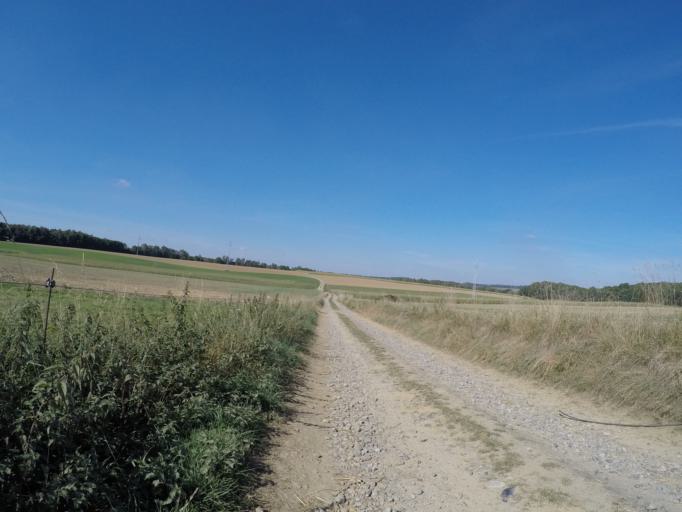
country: BE
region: Wallonia
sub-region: Province de Namur
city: Assesse
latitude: 50.3032
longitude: 5.0253
